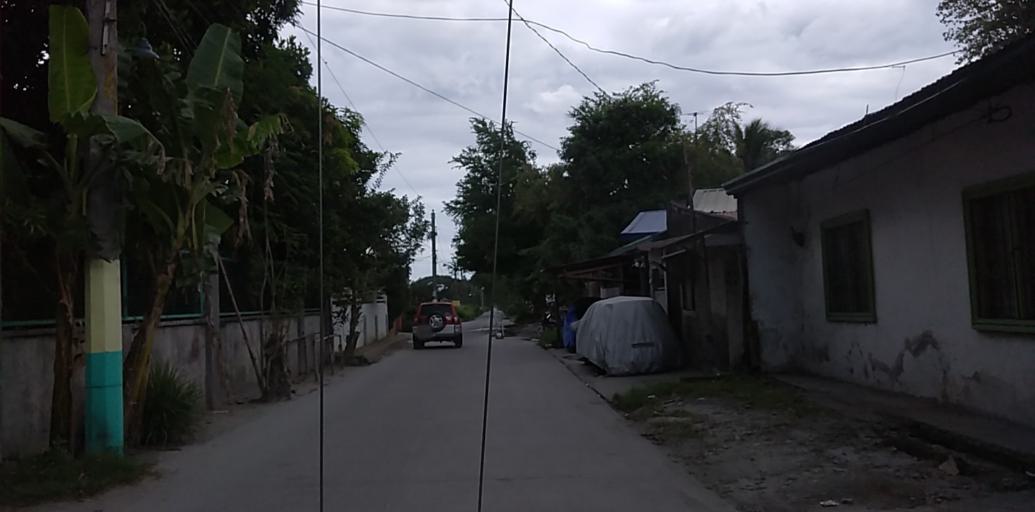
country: PH
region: Central Luzon
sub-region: Province of Pampanga
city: Porac
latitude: 15.0642
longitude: 120.5493
